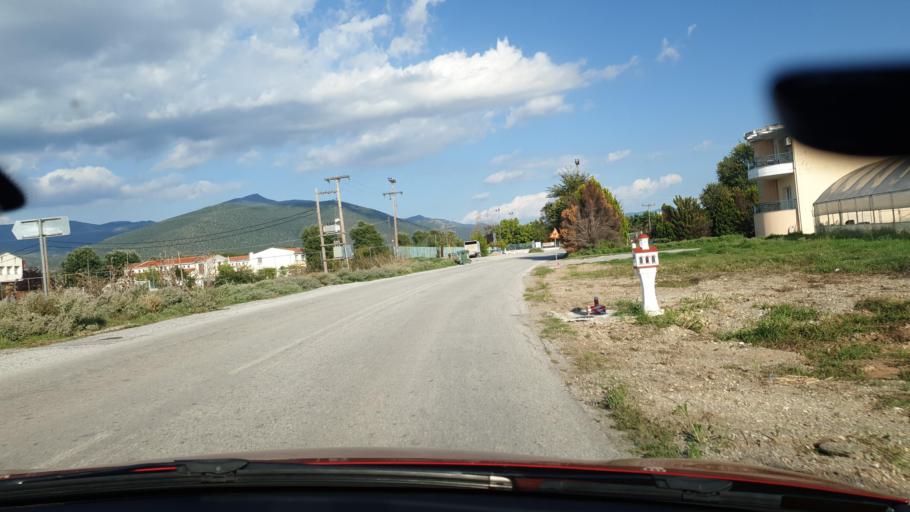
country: GR
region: Central Macedonia
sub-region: Nomos Thessalonikis
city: Vasilika
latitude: 40.4814
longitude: 23.1209
